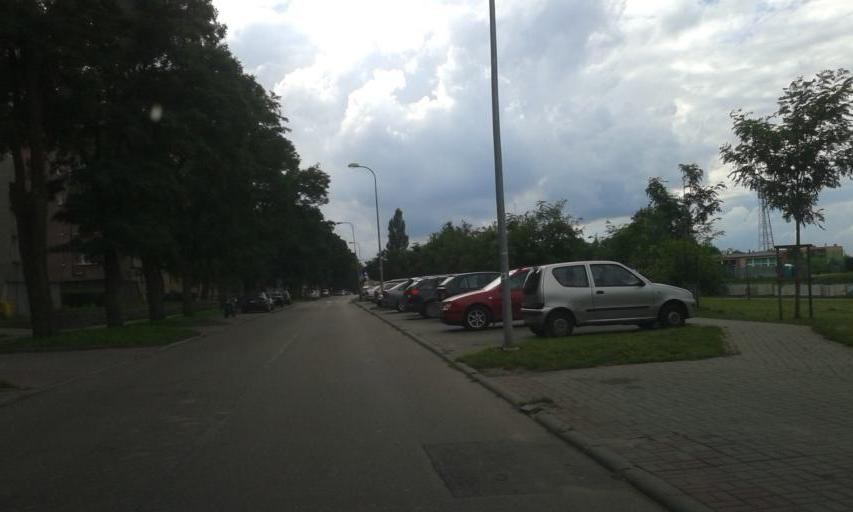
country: PL
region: West Pomeranian Voivodeship
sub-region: Powiat szczecinecki
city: Szczecinek
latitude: 53.7063
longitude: 16.7078
